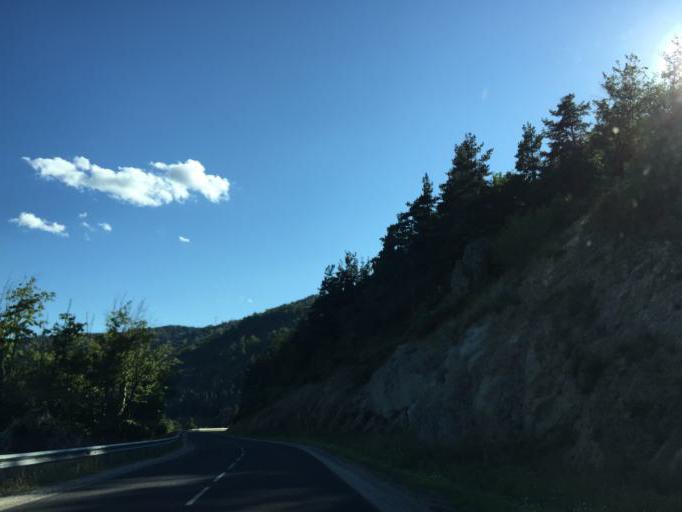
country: FR
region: Auvergne
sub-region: Departement de la Haute-Loire
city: Saugues
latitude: 44.9730
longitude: 3.6305
